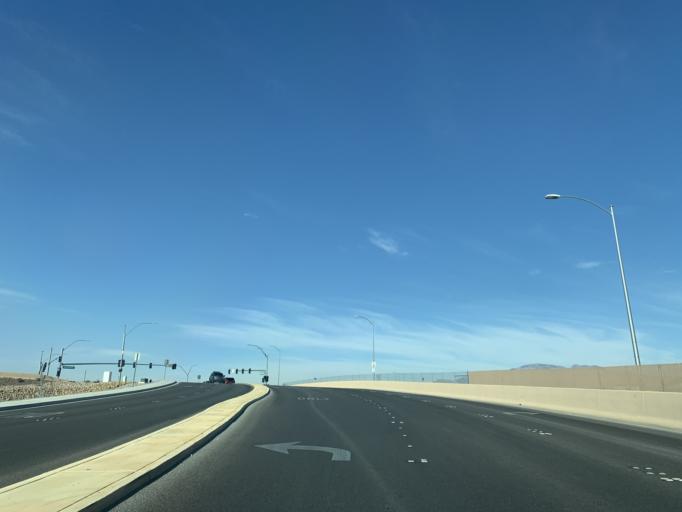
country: US
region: Nevada
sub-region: Clark County
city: Summerlin South
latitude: 36.3144
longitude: -115.2968
